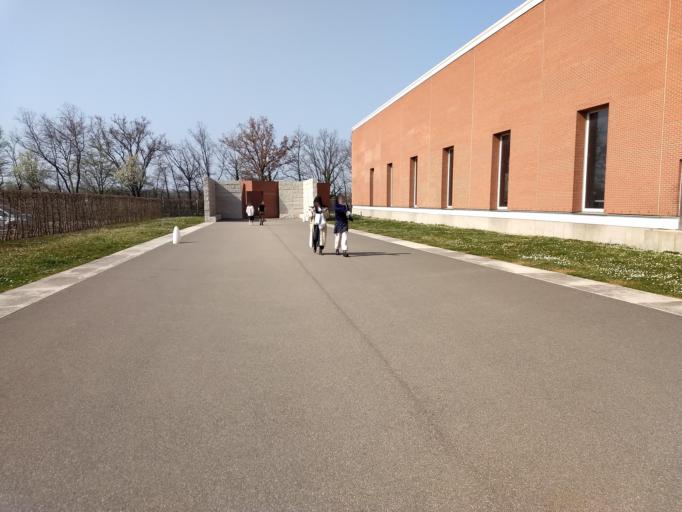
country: DE
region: Baden-Wuerttemberg
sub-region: Freiburg Region
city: Weil am Rhein
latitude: 47.6007
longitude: 7.6147
